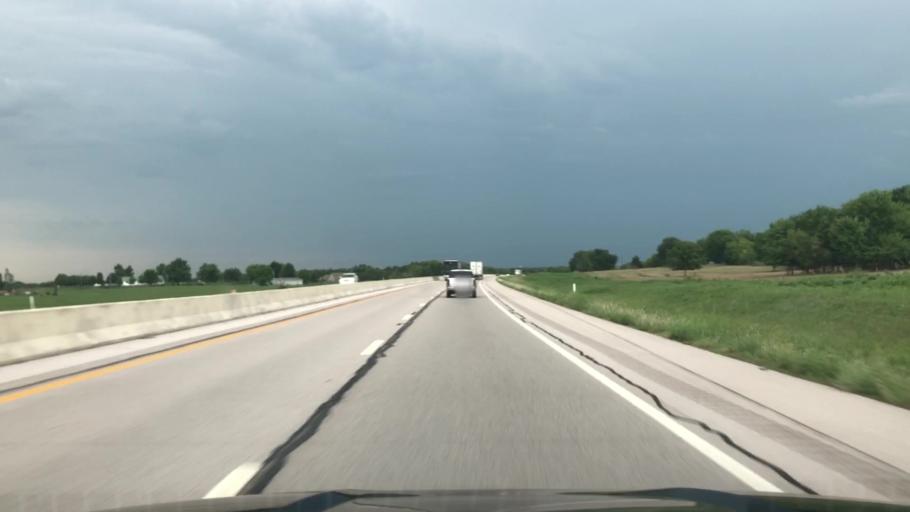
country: US
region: Oklahoma
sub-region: Rogers County
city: Bushyhead
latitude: 36.3550
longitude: -95.4578
